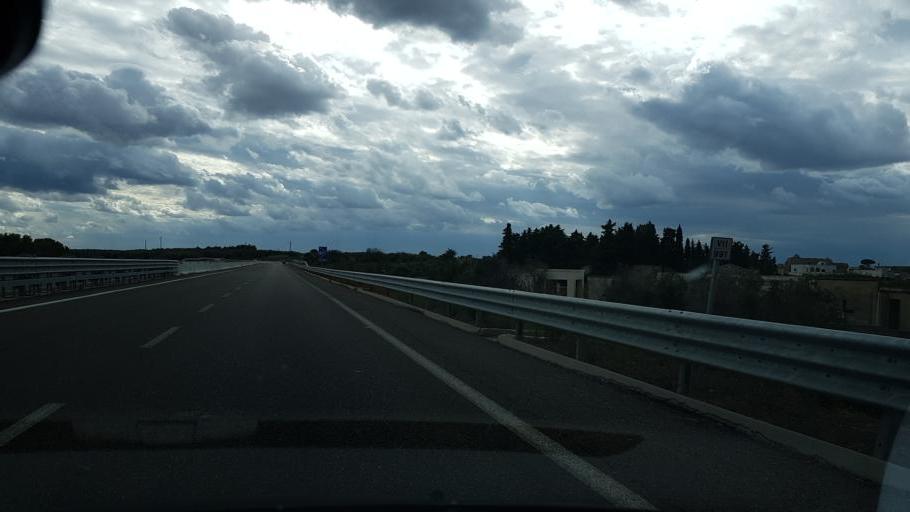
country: IT
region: Apulia
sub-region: Provincia di Lecce
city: Palmariggi
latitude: 40.1307
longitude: 18.3888
